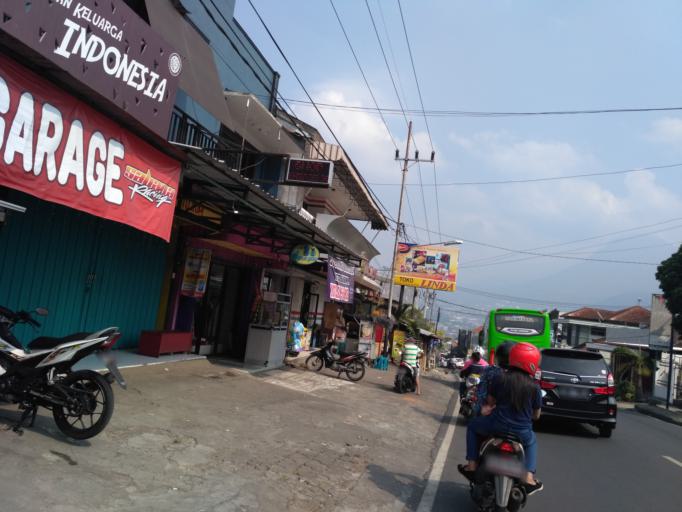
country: ID
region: East Java
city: Batu
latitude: -7.8510
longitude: 112.5279
